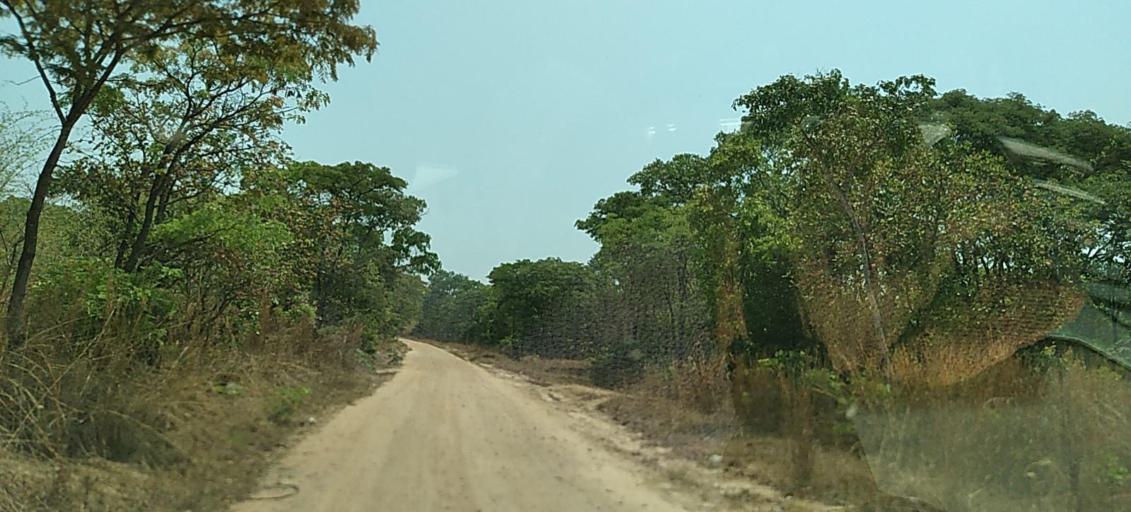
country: ZM
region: Copperbelt
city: Kalulushi
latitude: -12.9487
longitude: 28.1507
